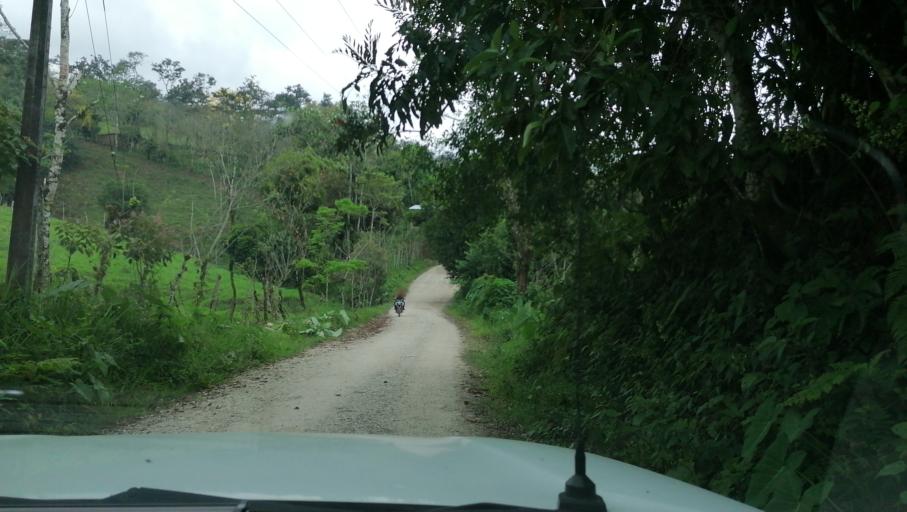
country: MX
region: Chiapas
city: Ocotepec
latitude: 17.2791
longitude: -93.2290
